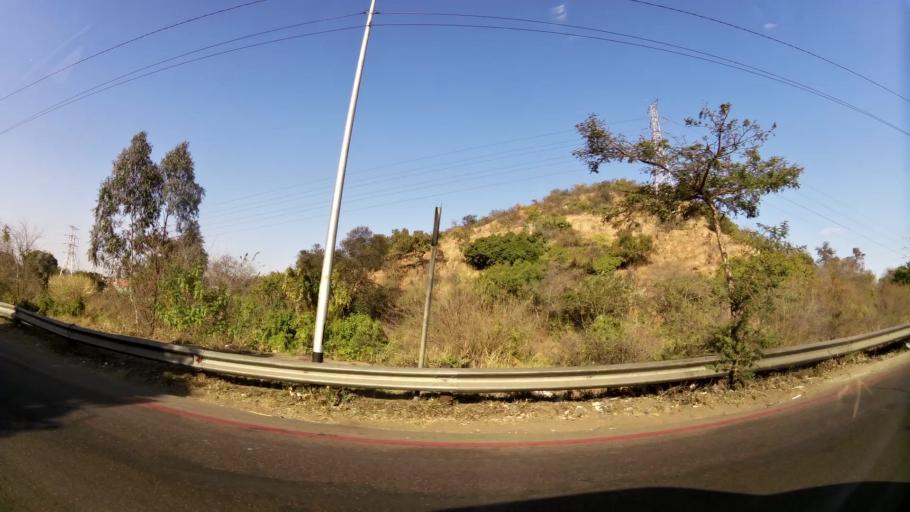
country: ZA
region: Gauteng
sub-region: City of Tshwane Metropolitan Municipality
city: Pretoria
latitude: -25.7281
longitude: 28.1699
